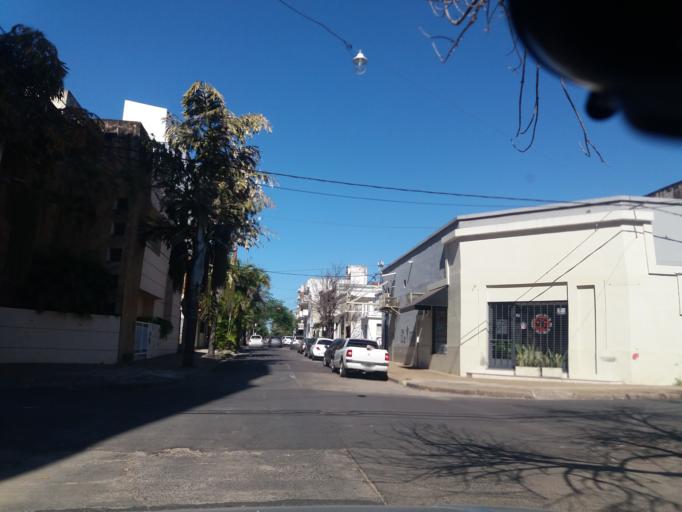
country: AR
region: Corrientes
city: Corrientes
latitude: -27.4669
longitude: -58.8442
